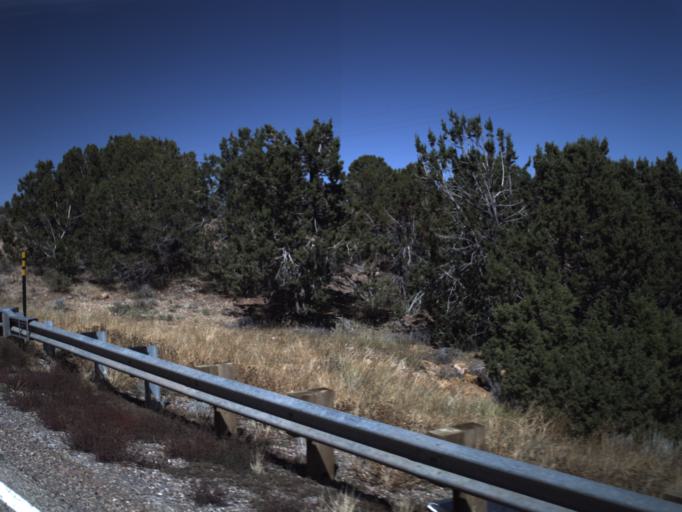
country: US
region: Utah
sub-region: Washington County
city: Enterprise
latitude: 37.5211
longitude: -113.6388
